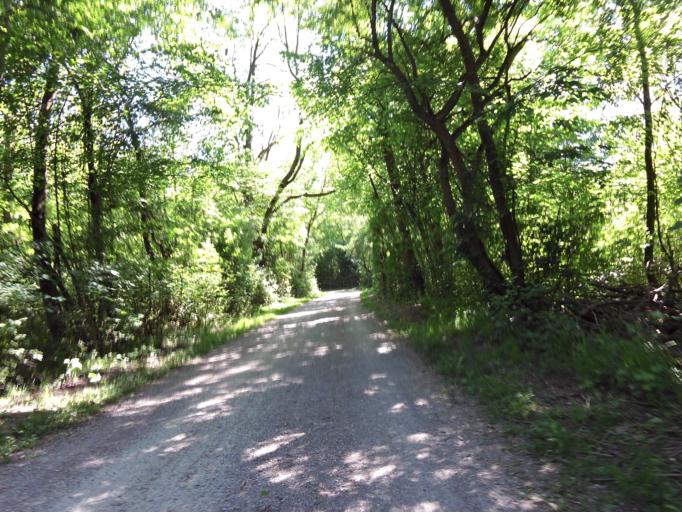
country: DE
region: Bavaria
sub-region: Upper Bavaria
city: Unterfoehring
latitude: 48.1959
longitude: 11.6323
